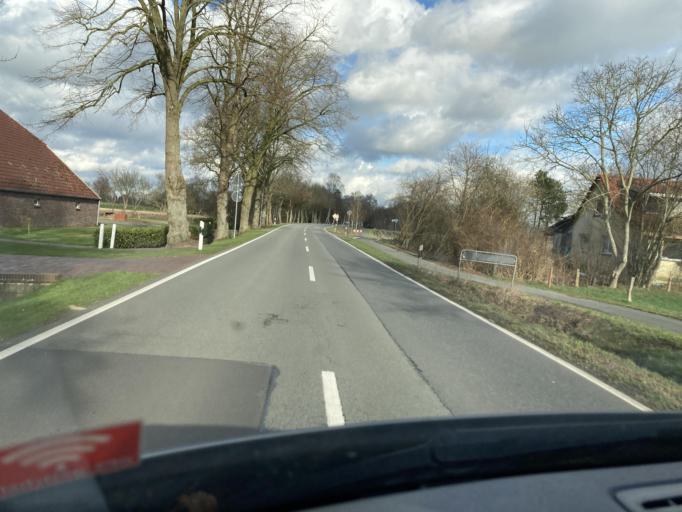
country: DE
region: Lower Saxony
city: Friedeburg
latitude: 53.3687
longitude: 7.8191
